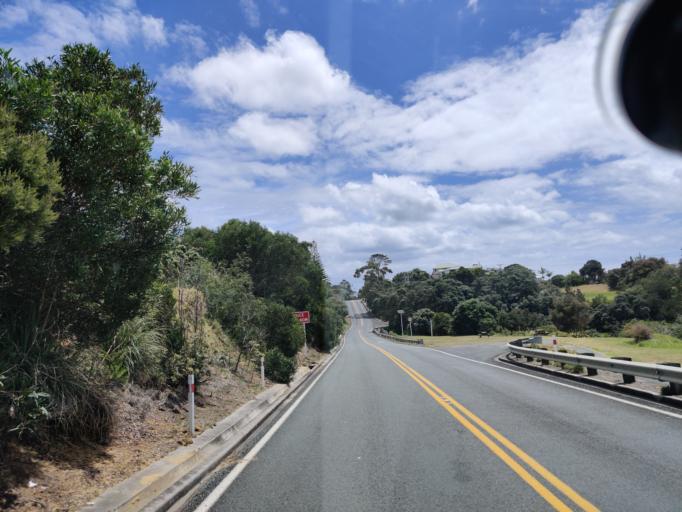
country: NZ
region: Northland
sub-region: Far North District
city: Kaitaia
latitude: -34.8123
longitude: 173.1166
